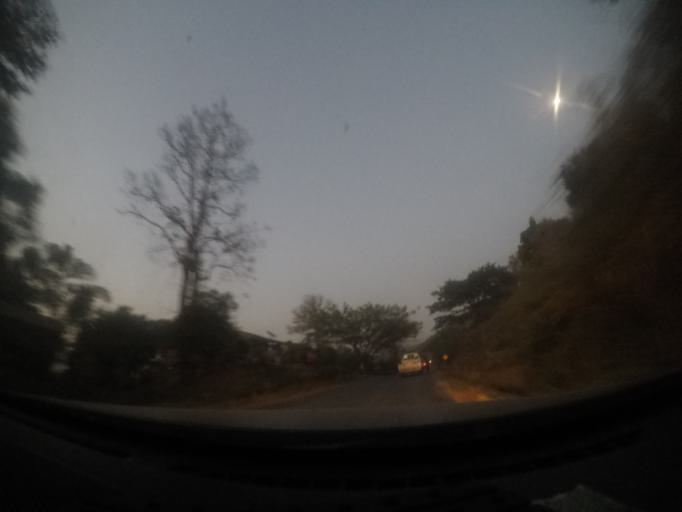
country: MM
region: Mandalay
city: Yamethin
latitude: 20.7053
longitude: 96.5108
